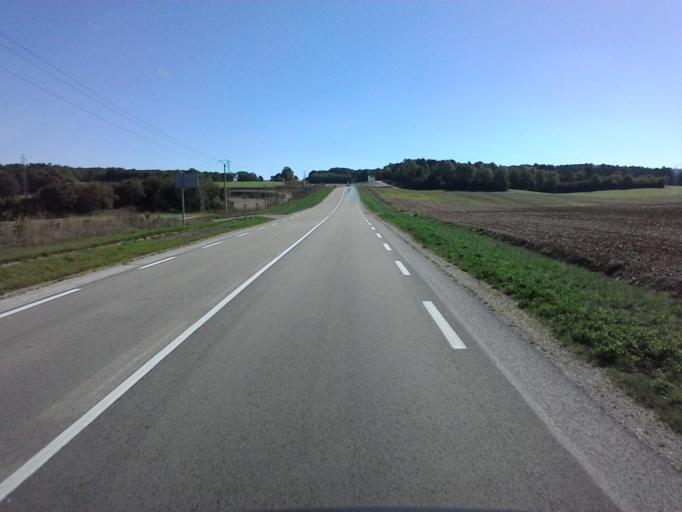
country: FR
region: Champagne-Ardenne
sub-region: Departement de la Haute-Marne
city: Chaumont
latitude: 48.1176
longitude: 5.1597
